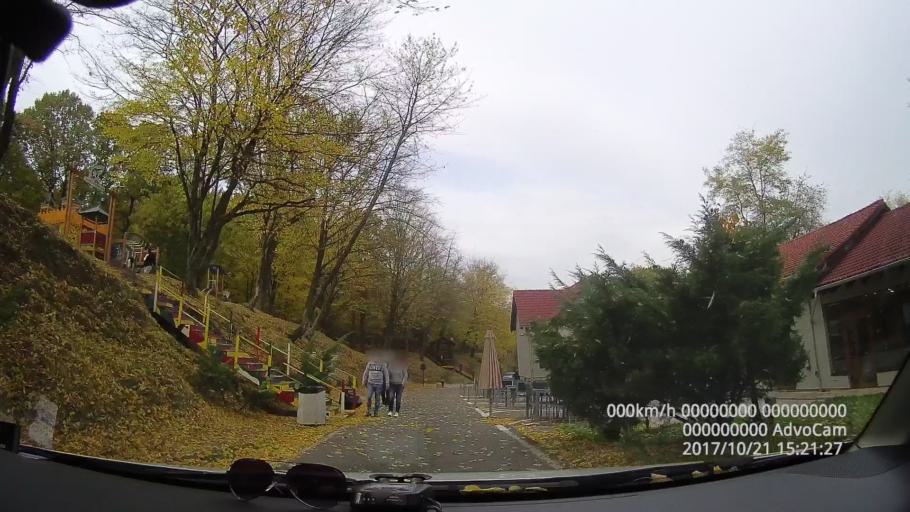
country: RO
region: Hunedoara
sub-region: Municipiul Deva
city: Cristur
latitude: 45.8526
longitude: 22.9692
